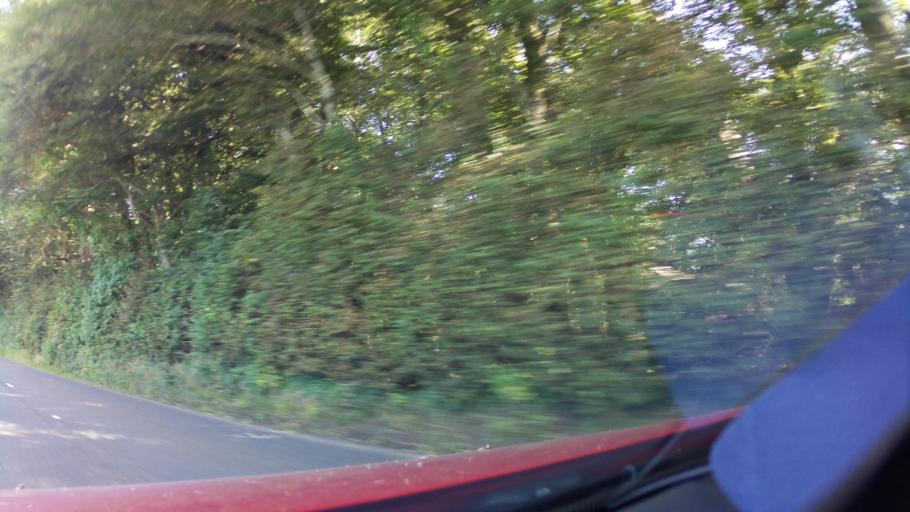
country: GB
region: England
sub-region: Devon
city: Tavistock
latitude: 50.5521
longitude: -4.1036
